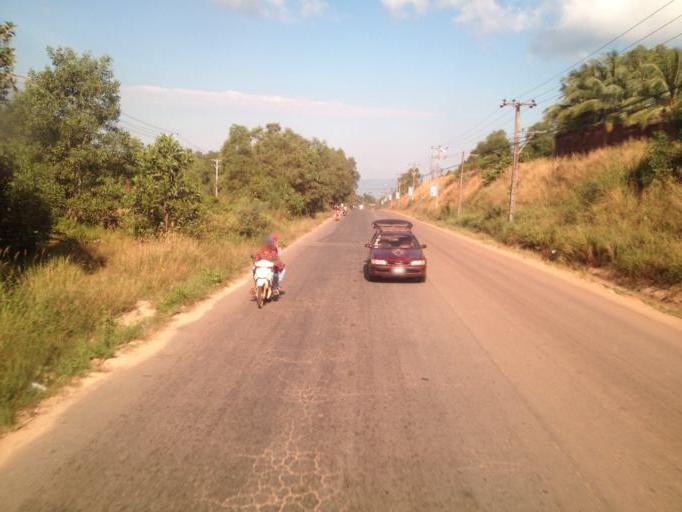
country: KH
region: Preah Sihanouk
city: Sihanoukville
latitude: 10.6383
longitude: 103.5313
